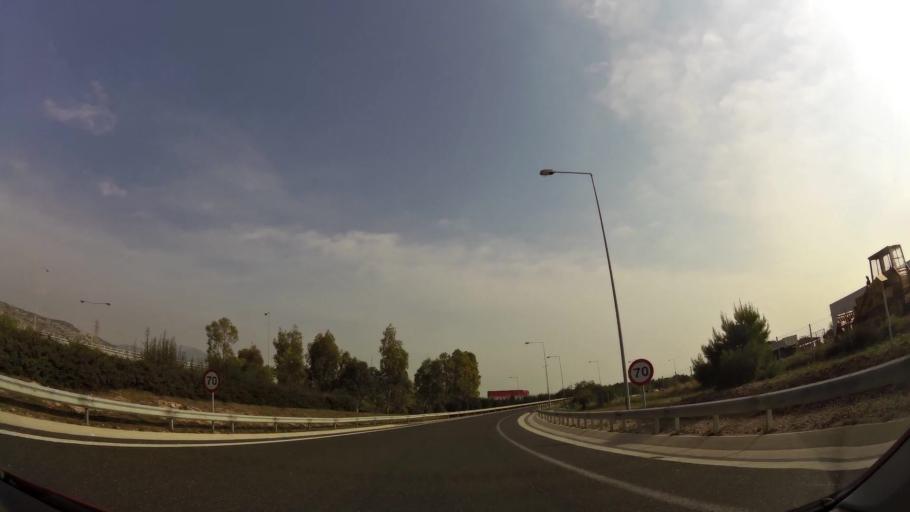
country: GR
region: Attica
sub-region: Nomarchia Dytikis Attikis
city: Ano Liosia
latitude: 38.0772
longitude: 23.6773
